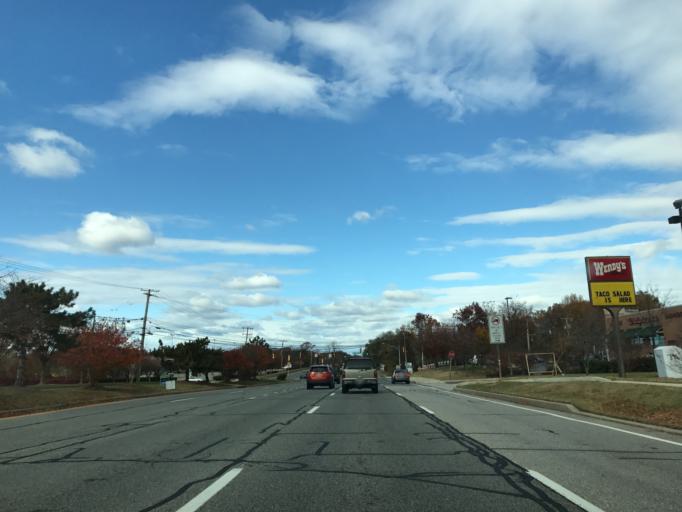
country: US
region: Maryland
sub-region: Anne Arundel County
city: South Gate
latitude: 39.1398
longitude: -76.6019
